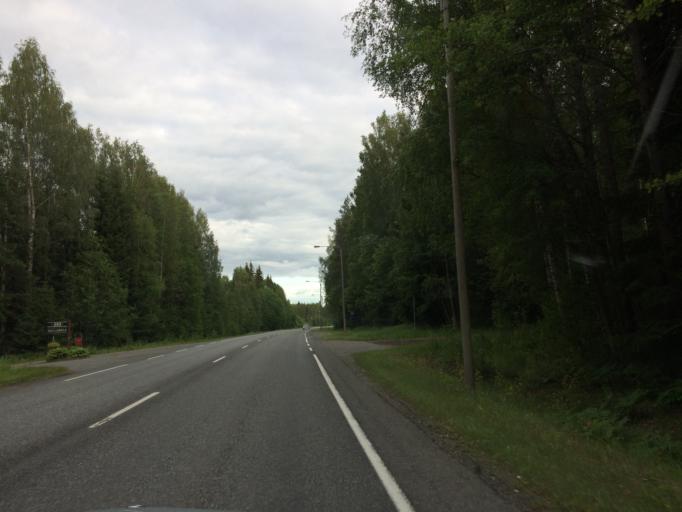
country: FI
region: Haeme
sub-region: Haemeenlinna
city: Haemeenlinna
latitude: 60.9451
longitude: 24.5152
